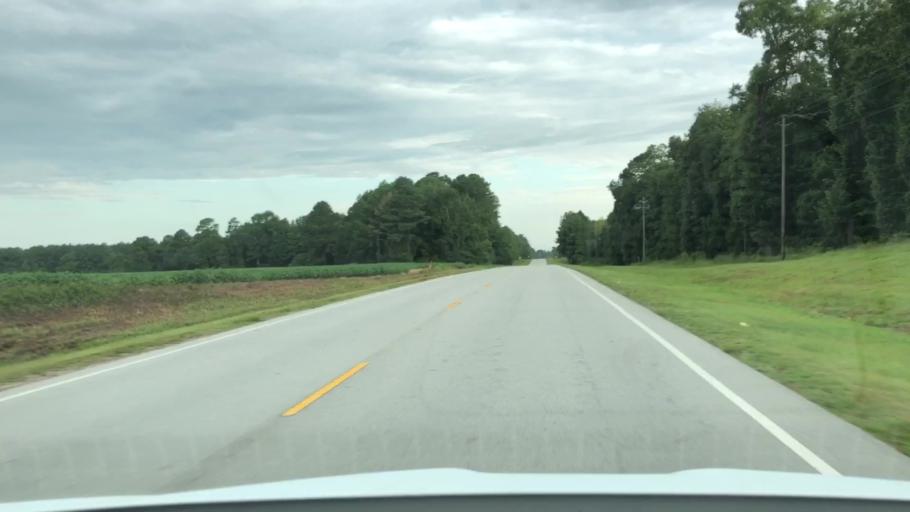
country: US
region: North Carolina
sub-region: Jones County
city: Trenton
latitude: 35.0080
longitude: -77.2840
